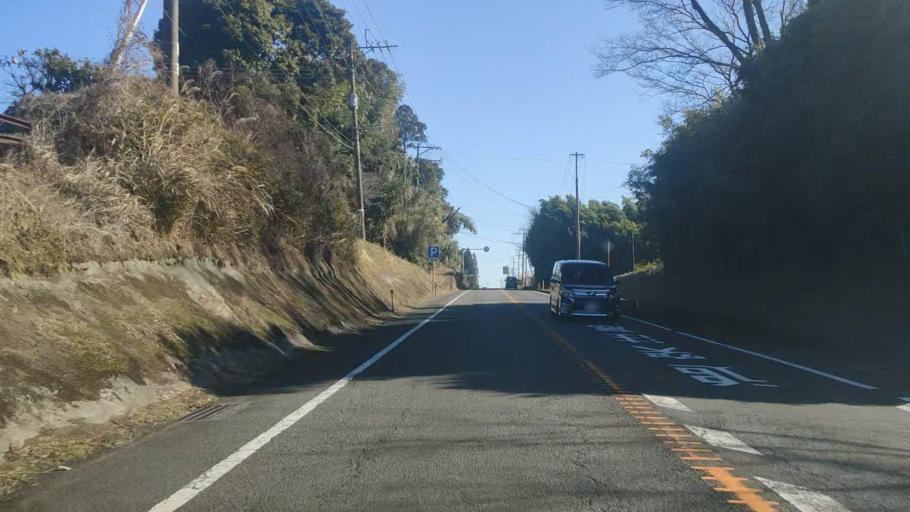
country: JP
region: Kagoshima
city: Sueyoshicho-ninokata
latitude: 31.6953
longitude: 130.9778
